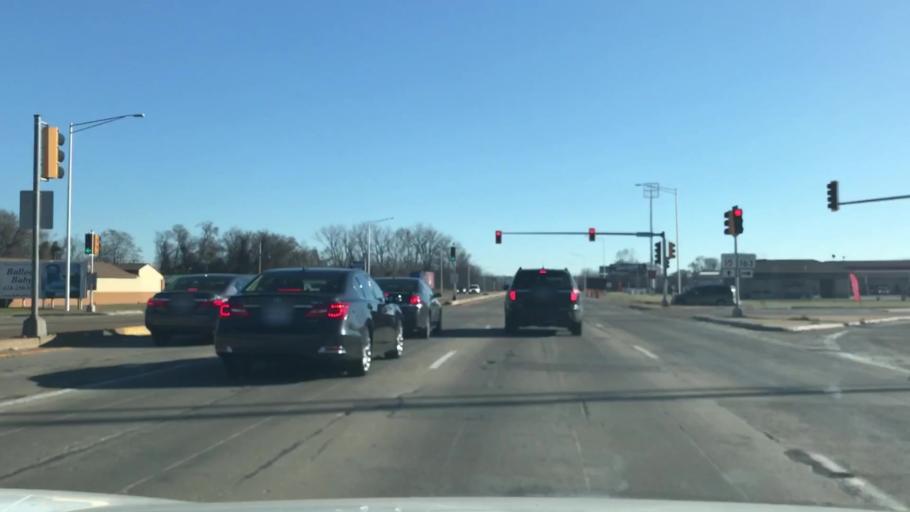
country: US
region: Illinois
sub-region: Saint Clair County
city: Alorton
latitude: 38.5918
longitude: -90.1186
